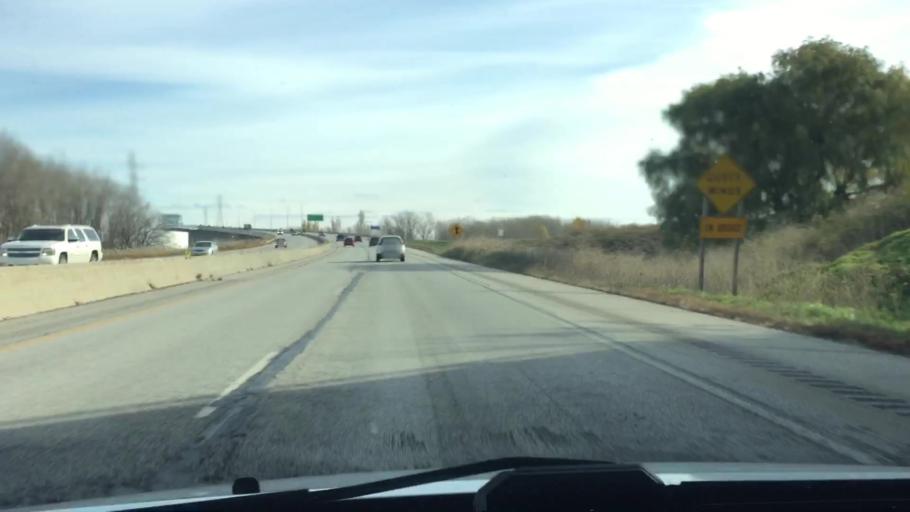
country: US
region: Wisconsin
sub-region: Brown County
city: Green Bay
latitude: 44.5394
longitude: -88.0246
